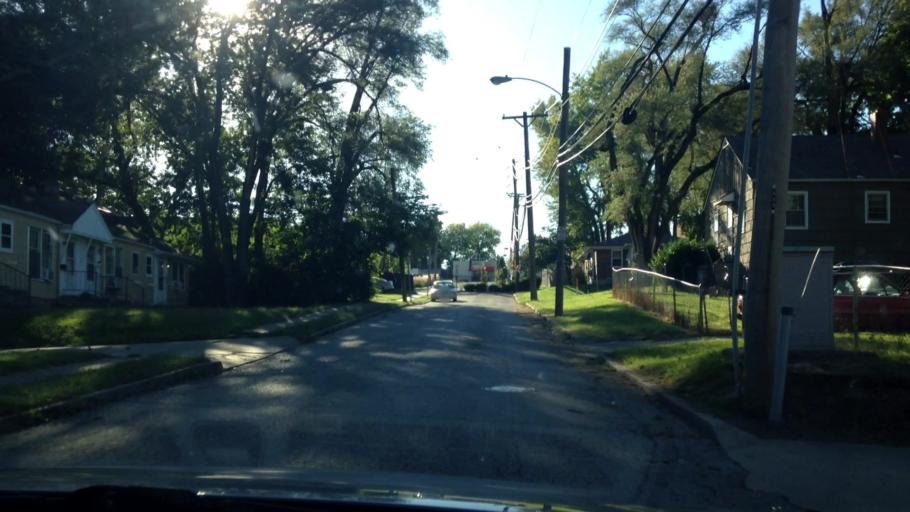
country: US
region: Kansas
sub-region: Johnson County
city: Westwood
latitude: 39.0511
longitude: -94.6100
